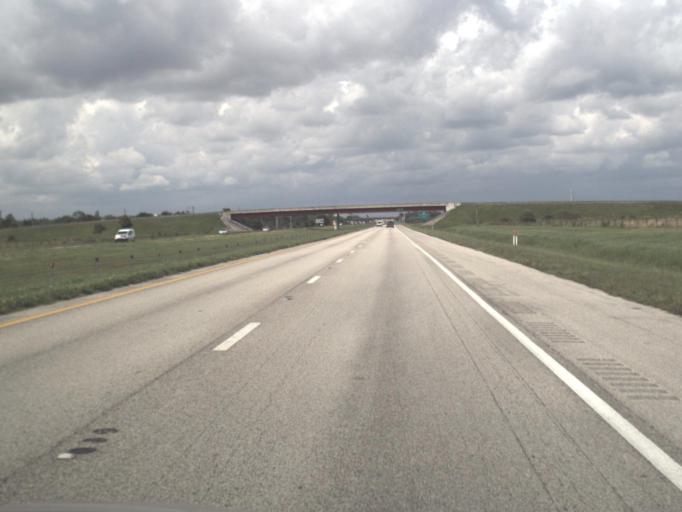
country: US
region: Florida
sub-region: Charlotte County
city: Punta Gorda
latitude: 26.9145
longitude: -82.0113
